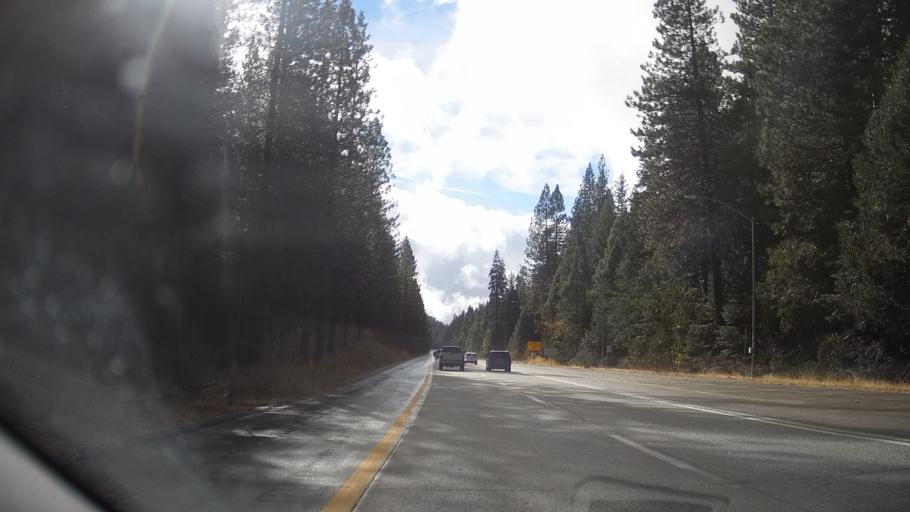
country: US
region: California
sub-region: Placer County
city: Foresthill
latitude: 39.2541
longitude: -120.7375
